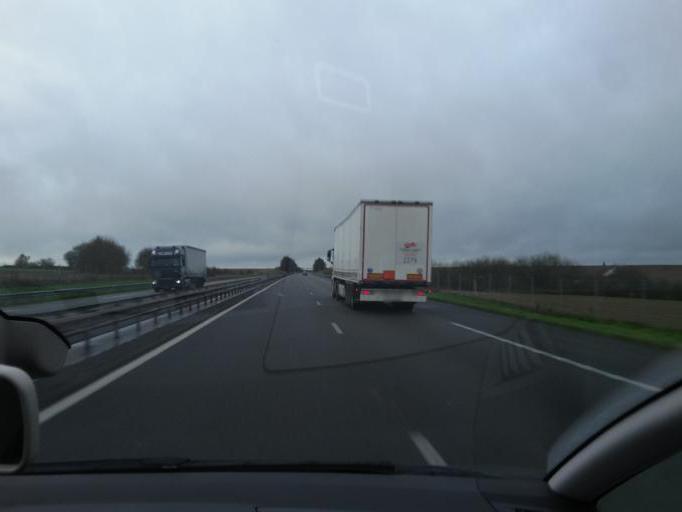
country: FR
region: Nord-Pas-de-Calais
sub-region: Departement du Pas-de-Calais
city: Hermies
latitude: 50.0905
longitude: 3.0457
